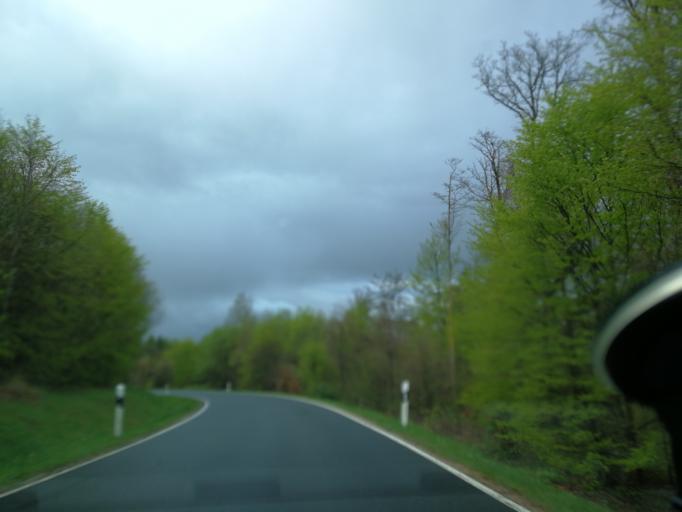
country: DE
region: Rheinland-Pfalz
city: Nohn
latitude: 50.3144
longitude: 6.7960
